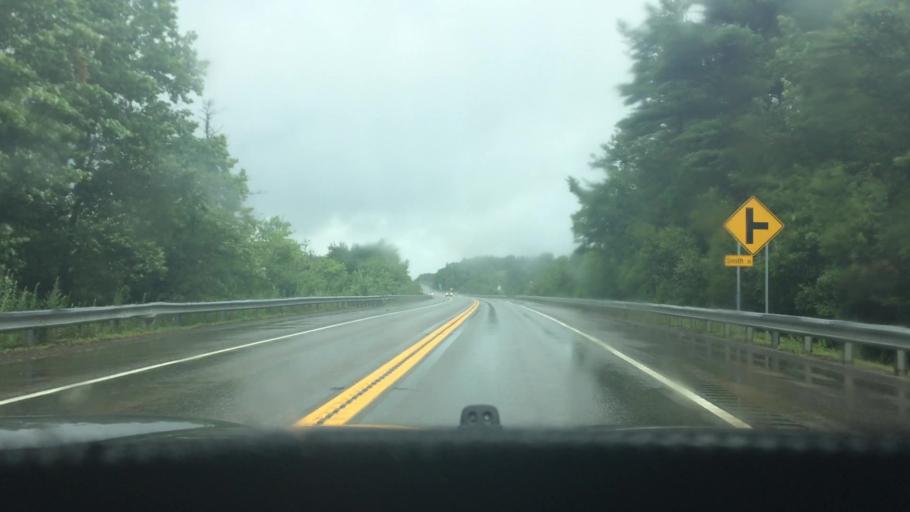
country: US
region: Massachusetts
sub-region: Worcester County
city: South Ashburnham
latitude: 42.5835
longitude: -71.9542
